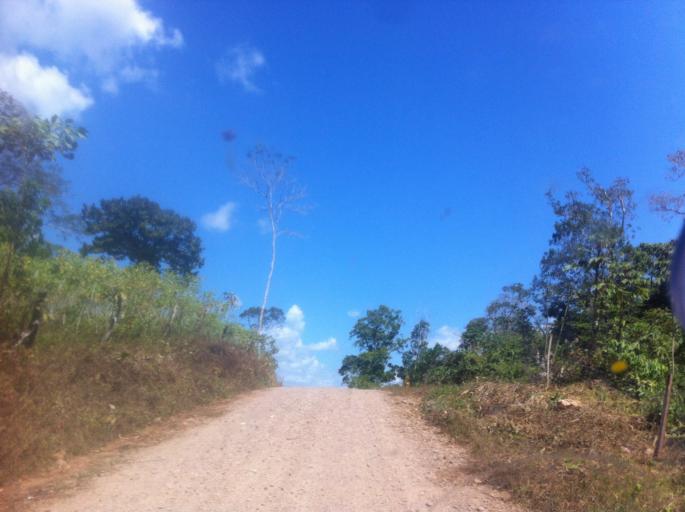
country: CR
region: Alajuela
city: Los Chiles
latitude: 11.2457
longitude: -84.4650
